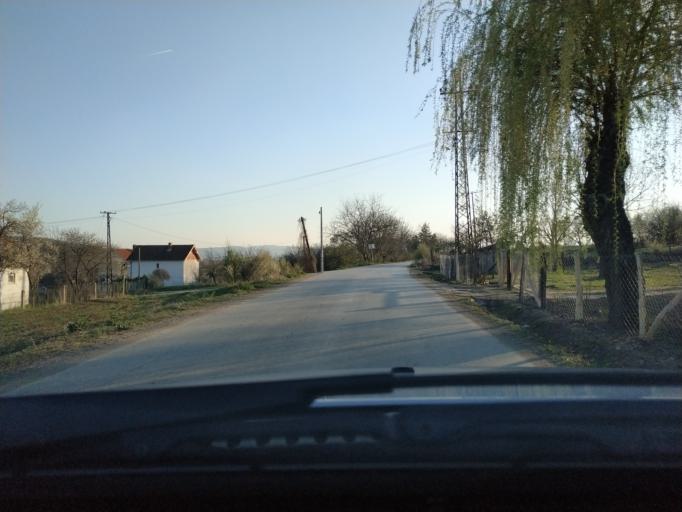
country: RS
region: Central Serbia
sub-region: Nisavski Okrug
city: Aleksinac
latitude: 43.5041
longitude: 21.7937
